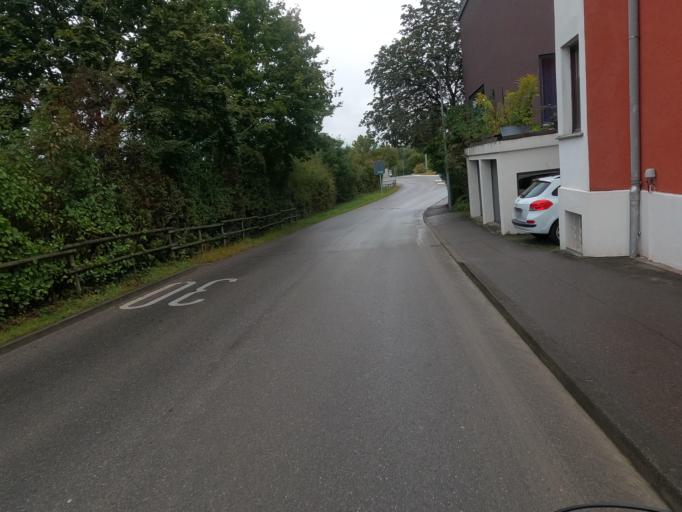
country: DE
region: Baden-Wuerttemberg
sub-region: Freiburg Region
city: Radolfzell am Bodensee
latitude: 47.7378
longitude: 8.9777
